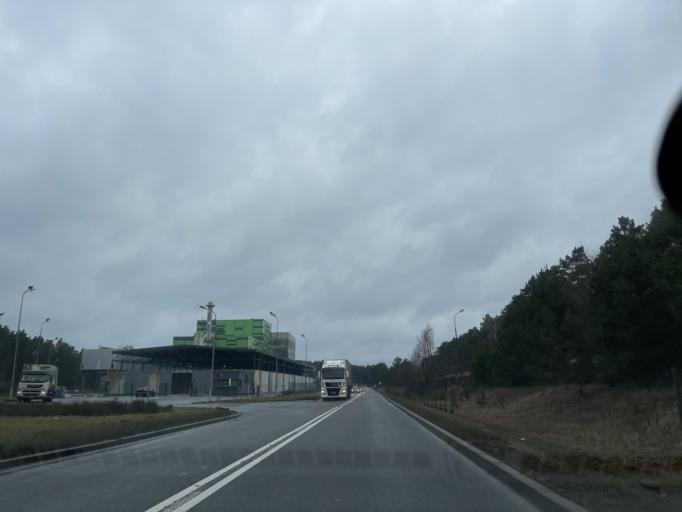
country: PL
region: Kujawsko-Pomorskie
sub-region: Powiat bydgoski
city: Nowa Wies Wielka
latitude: 53.0674
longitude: 18.0861
